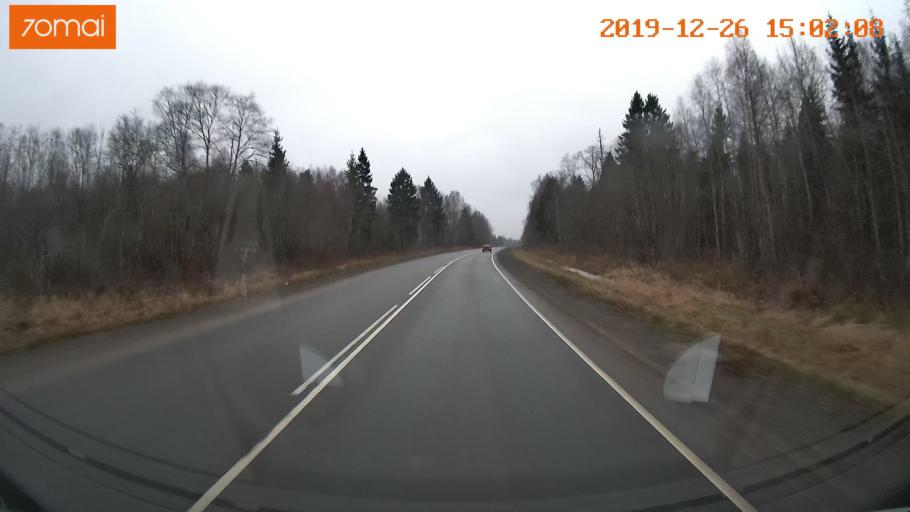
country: RU
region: Jaroslavl
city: Rybinsk
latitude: 58.2295
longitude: 38.8733
